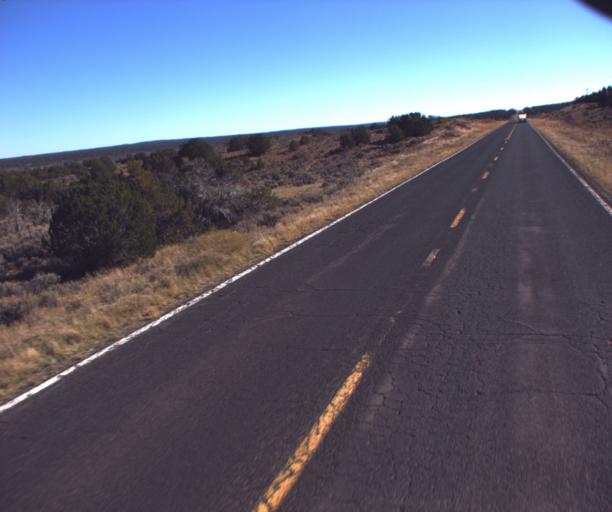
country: US
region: Arizona
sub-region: Apache County
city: Ganado
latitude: 35.5375
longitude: -109.5293
